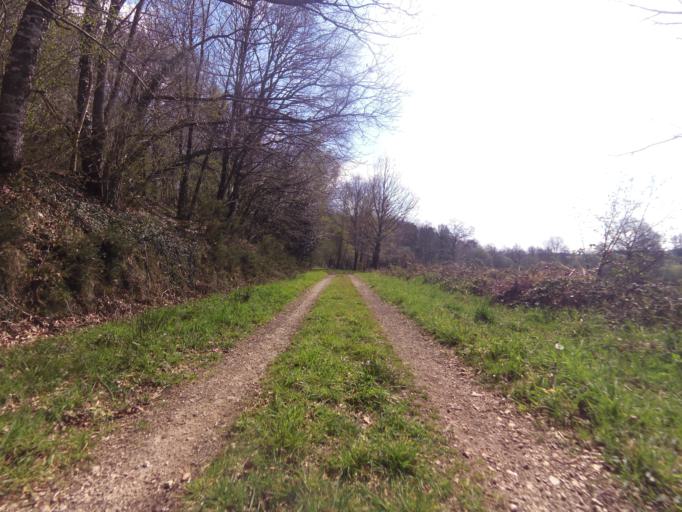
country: FR
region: Brittany
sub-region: Departement du Morbihan
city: Molac
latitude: 47.7184
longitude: -2.4101
